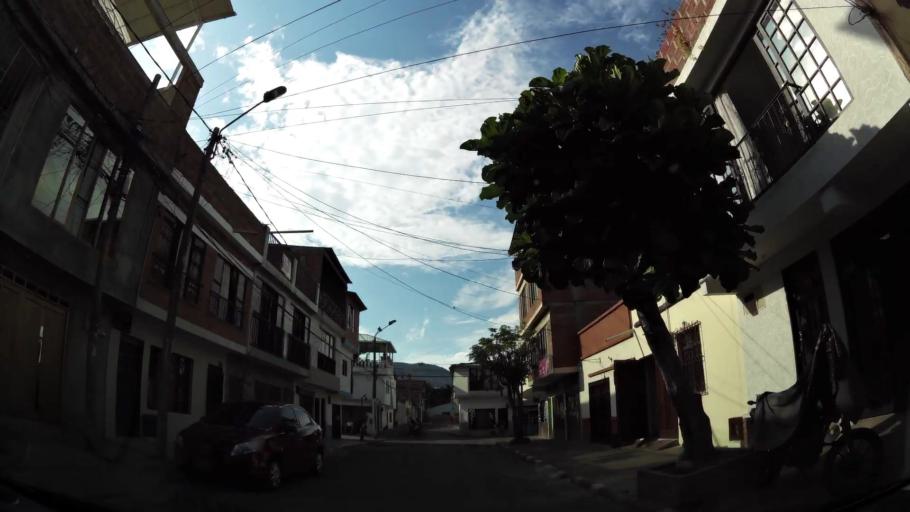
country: CO
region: Valle del Cauca
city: Cali
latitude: 3.4726
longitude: -76.5134
